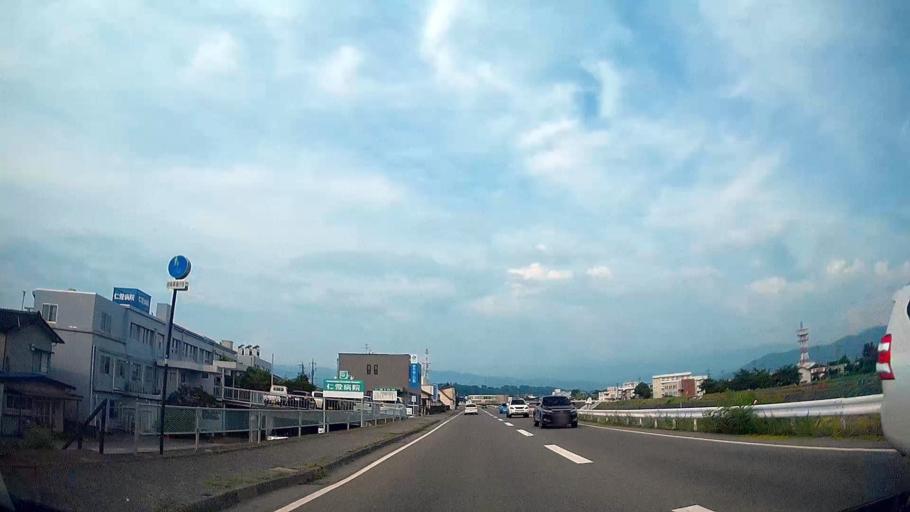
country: JP
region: Nagano
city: Ina
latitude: 35.8353
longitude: 137.9570
